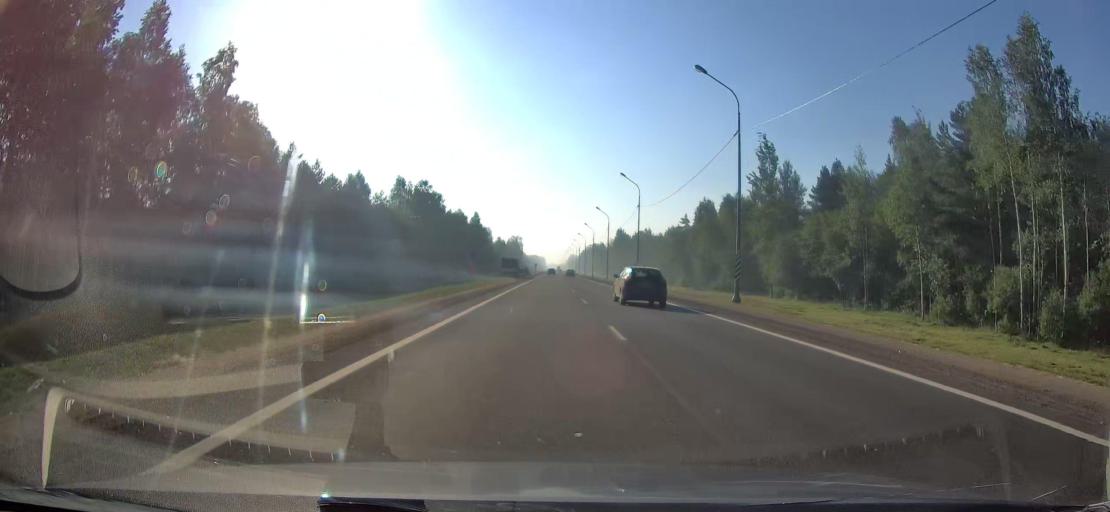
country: RU
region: Leningrad
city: Sinyavino
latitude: 59.8943
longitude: 31.1310
